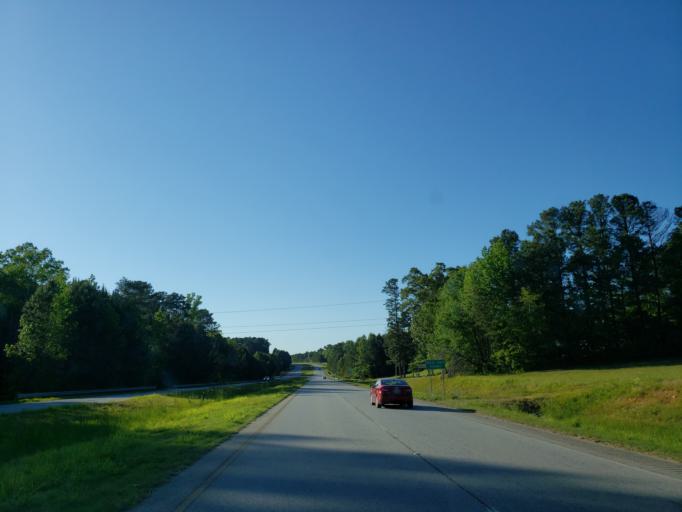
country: US
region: Georgia
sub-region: Haralson County
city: Buchanan
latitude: 33.9006
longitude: -85.2335
